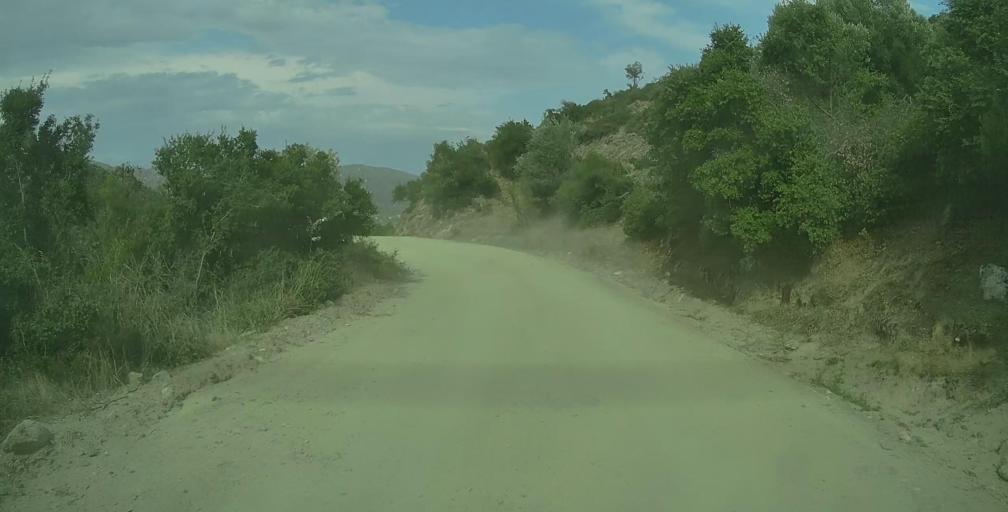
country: GR
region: Central Macedonia
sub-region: Nomos Chalkidikis
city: Sykia
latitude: 40.0190
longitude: 23.9392
